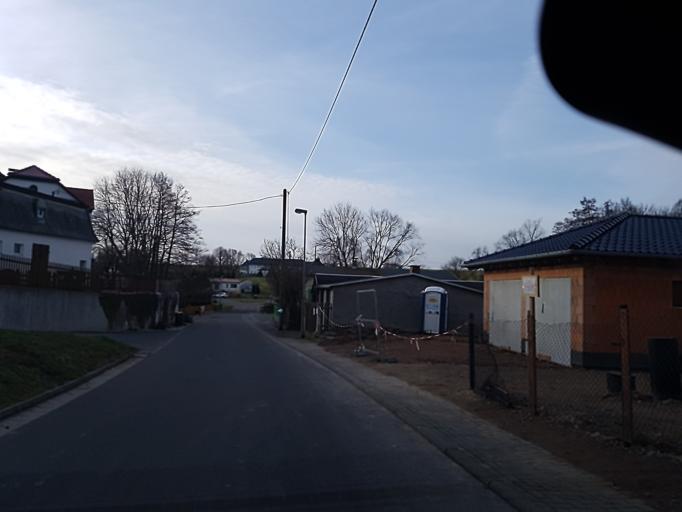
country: DE
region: Saxony
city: Bockelwitz
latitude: 51.1680
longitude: 12.9802
